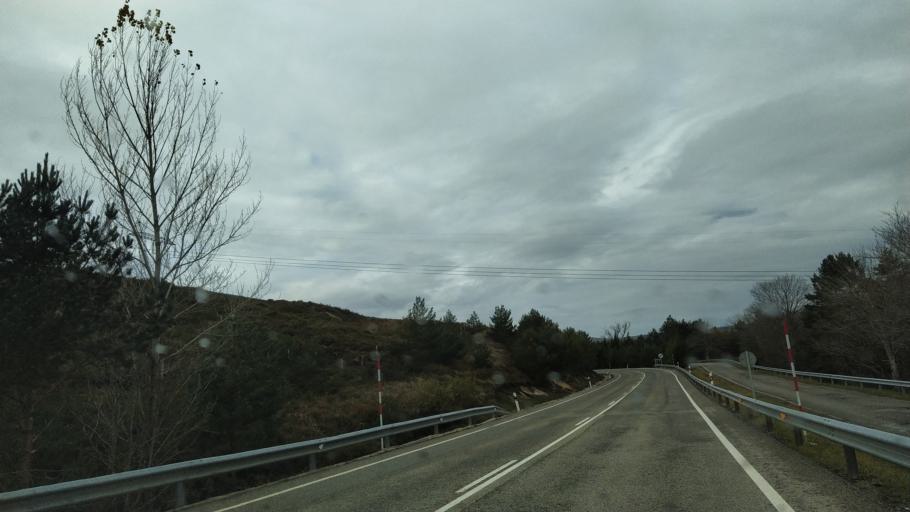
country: ES
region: Castille and Leon
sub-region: Provincia de Burgos
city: Arija
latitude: 42.9975
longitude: -3.8373
